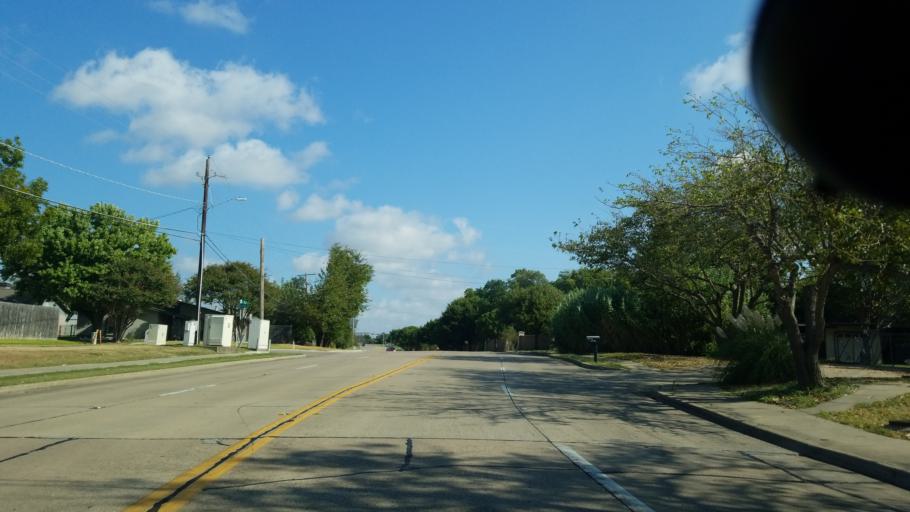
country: US
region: Texas
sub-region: Dallas County
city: Grand Prairie
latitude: 32.6957
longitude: -96.9943
